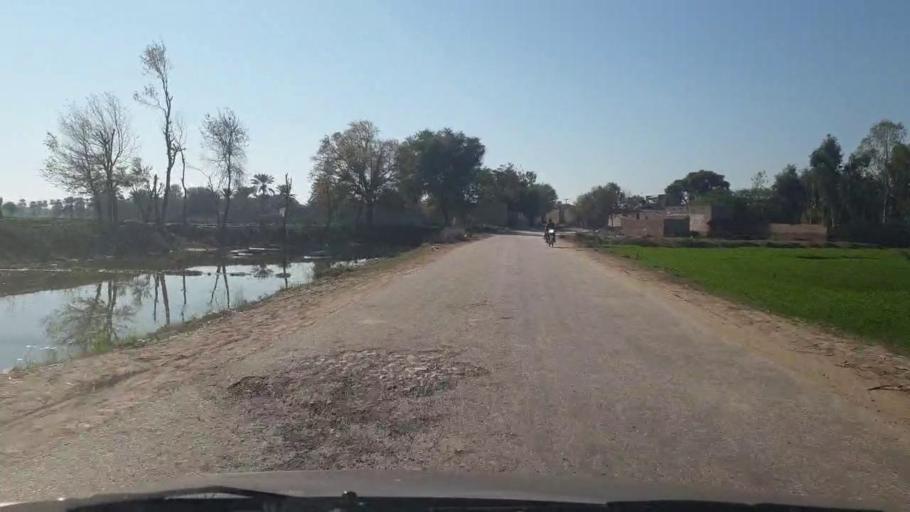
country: PK
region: Sindh
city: Bozdar
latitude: 27.0972
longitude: 68.6282
